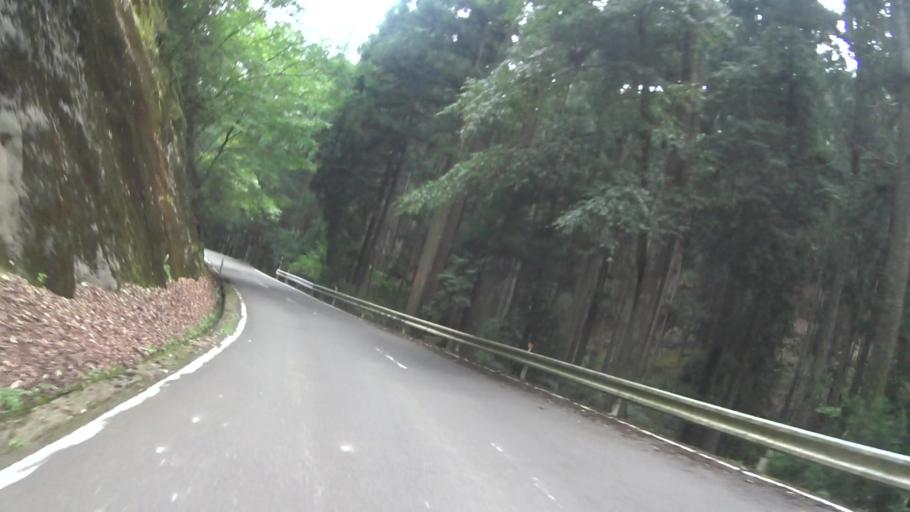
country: JP
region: Kyoto
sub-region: Kyoto-shi
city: Kamigyo-ku
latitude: 35.2031
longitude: 135.6764
